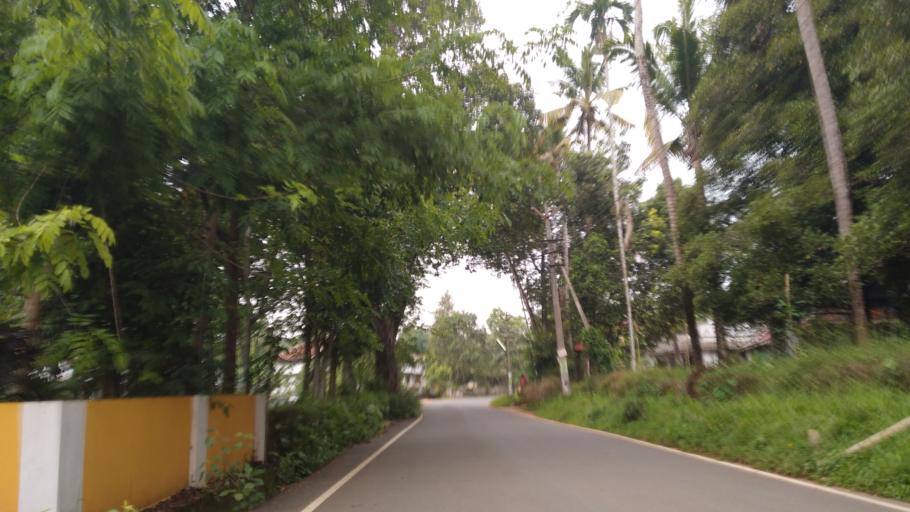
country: IN
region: Kerala
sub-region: Ernakulam
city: Perumbavoor
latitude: 10.0548
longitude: 76.5063
